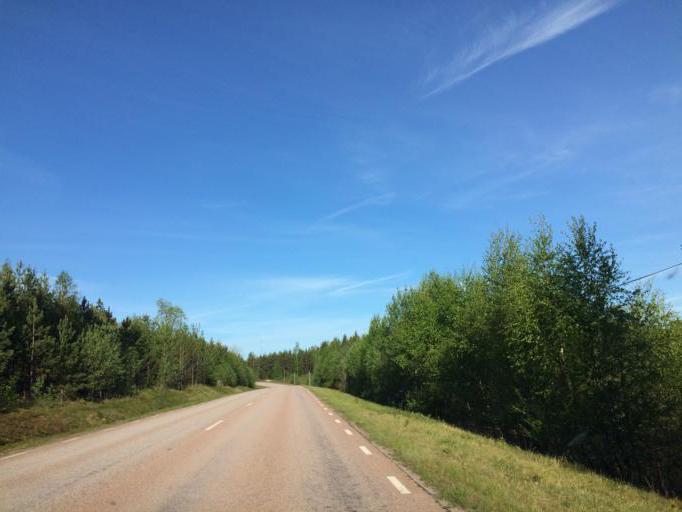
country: SE
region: Soedermanland
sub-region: Eskilstuna Kommun
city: Kvicksund
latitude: 59.4224
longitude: 16.3212
